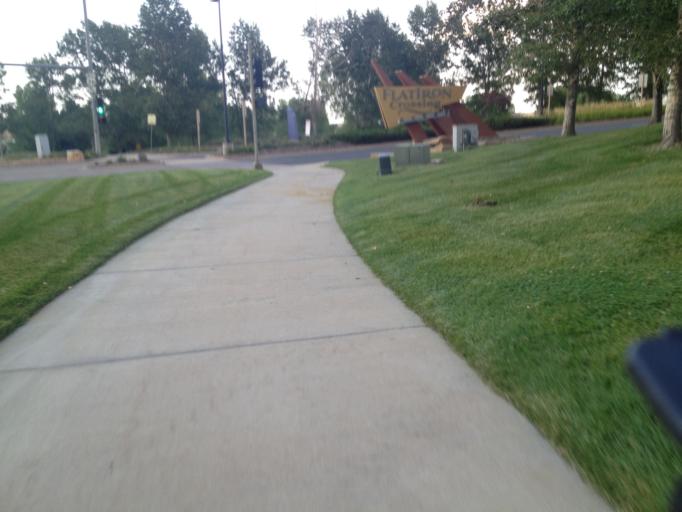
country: US
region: Colorado
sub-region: Boulder County
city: Superior
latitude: 39.9362
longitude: -105.1368
